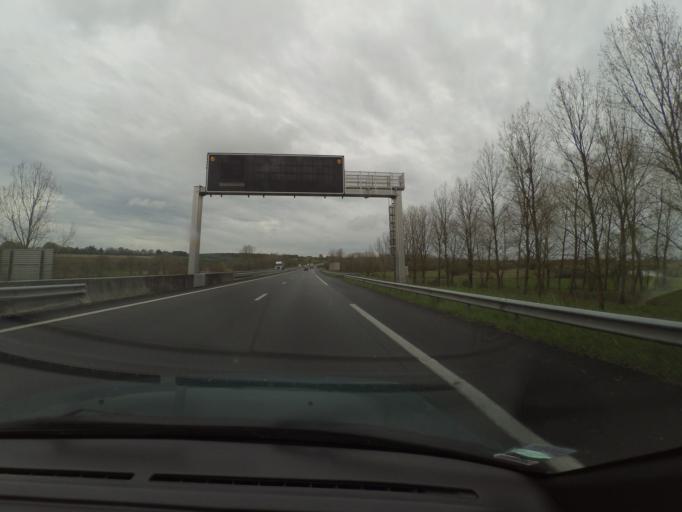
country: FR
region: Pays de la Loire
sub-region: Departement de Maine-et-Loire
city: Durtal
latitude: 47.6514
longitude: -0.2733
